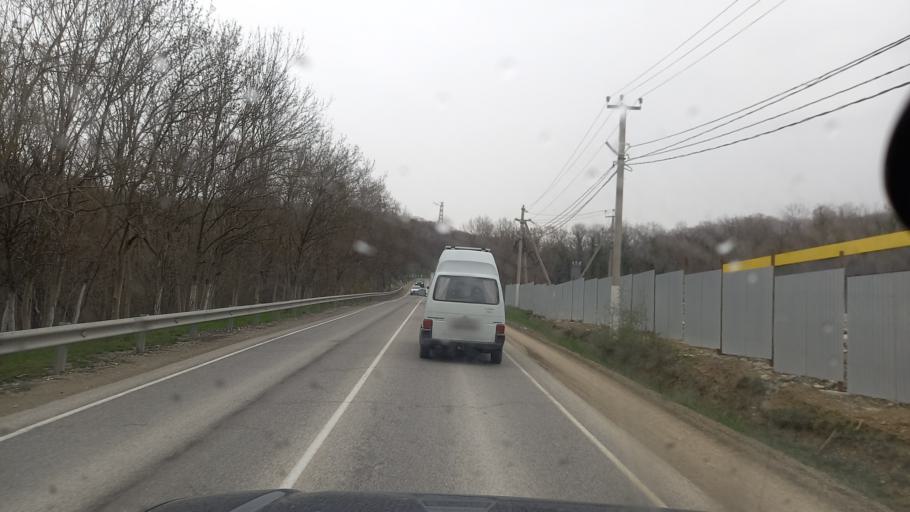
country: RU
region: Krasnodarskiy
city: Gayduk
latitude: 44.7375
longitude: 37.6772
